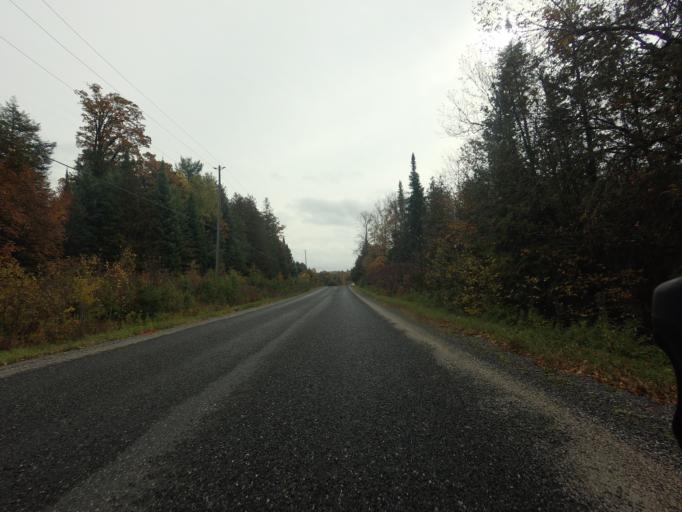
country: CA
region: Ontario
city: Perth
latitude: 45.1244
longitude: -76.5238
